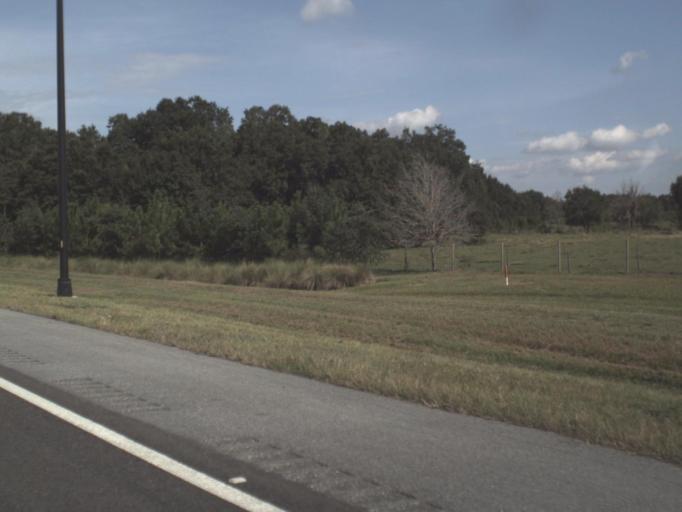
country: US
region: Florida
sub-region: Polk County
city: Polk City
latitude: 28.1241
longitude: -81.8363
